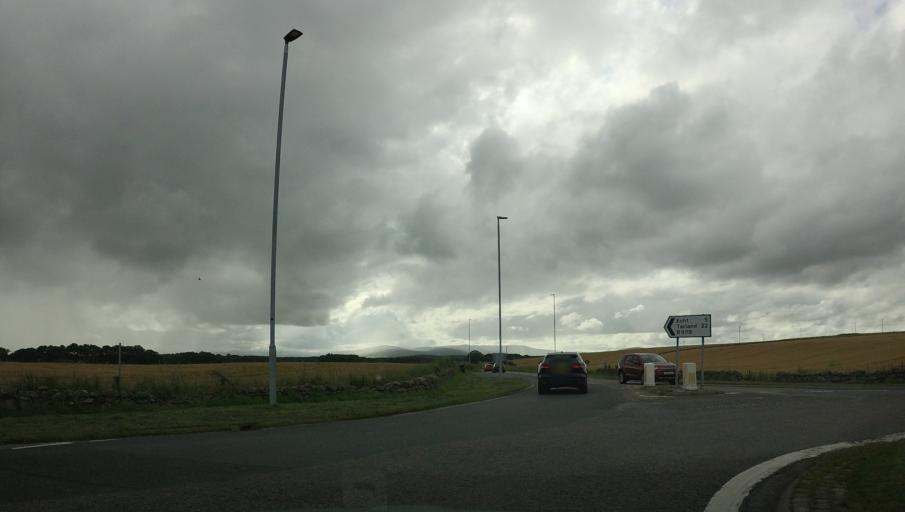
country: GB
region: Scotland
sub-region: Aberdeenshire
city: Westhill
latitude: 57.1426
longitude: -2.3096
